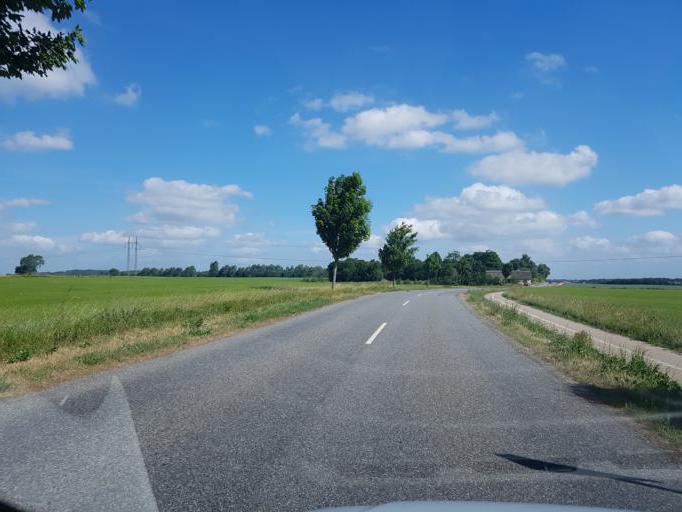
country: DK
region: Zealand
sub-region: Lejre Kommune
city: Osted
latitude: 55.5754
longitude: 11.9663
